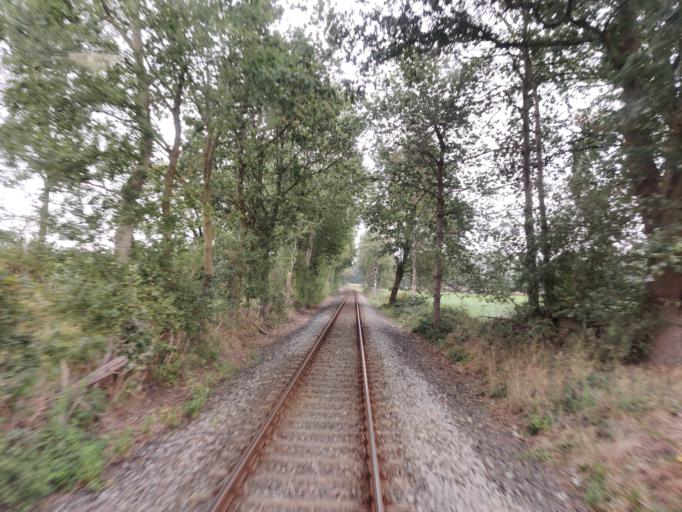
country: DE
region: Lower Saxony
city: Deinste
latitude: 53.5434
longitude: 9.4549
